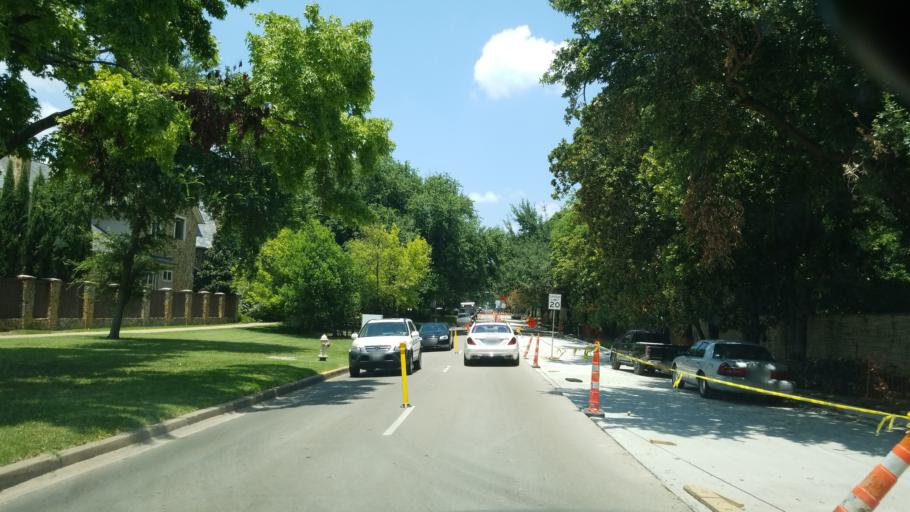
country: US
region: Texas
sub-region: Dallas County
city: Highland Park
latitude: 32.8305
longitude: -96.8045
